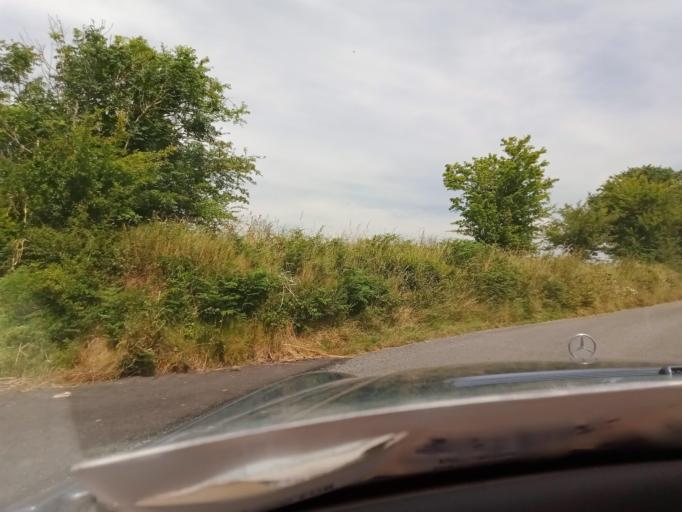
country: IE
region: Leinster
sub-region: Kilkenny
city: Mooncoin
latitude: 52.2529
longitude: -7.2109
